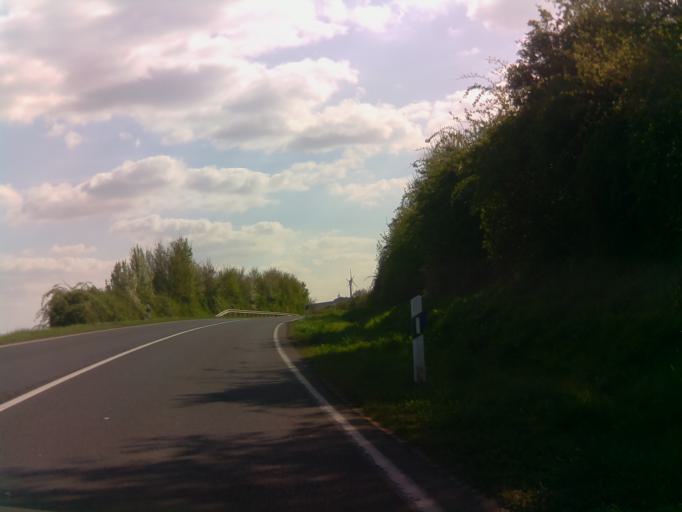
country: DE
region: Rheinland-Pfalz
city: Dienheim
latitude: 49.8286
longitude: 8.3483
